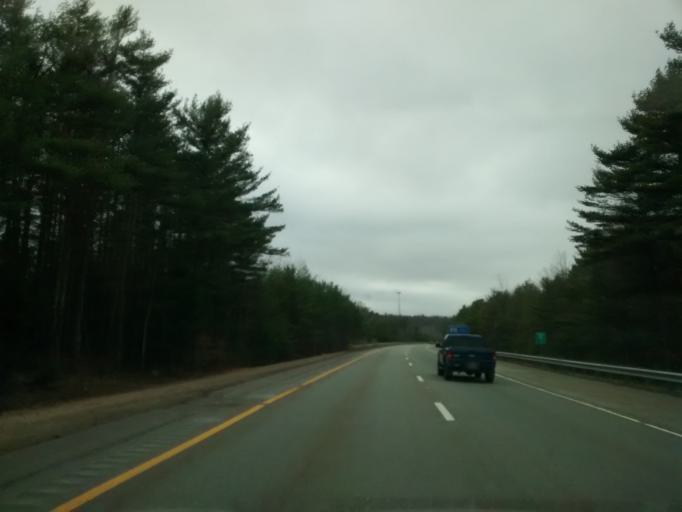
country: US
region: Massachusetts
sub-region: Worcester County
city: Templeton
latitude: 42.5688
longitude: -72.0977
